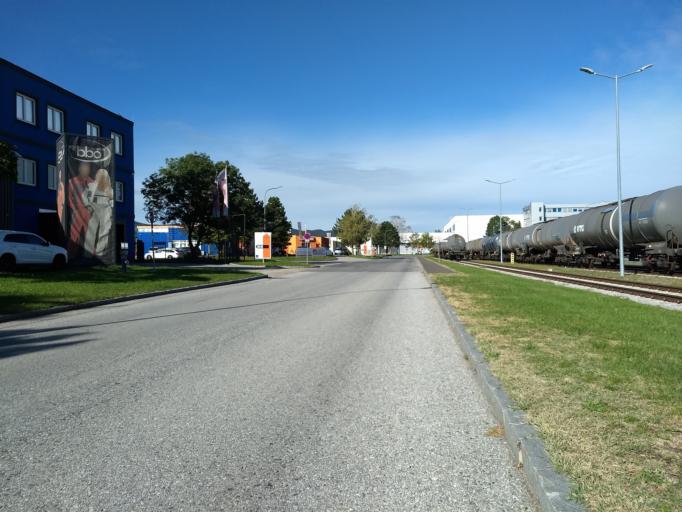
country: AT
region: Lower Austria
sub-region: Politischer Bezirk Modling
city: Neu-Guntramsdorf
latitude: 48.0680
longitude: 16.3280
